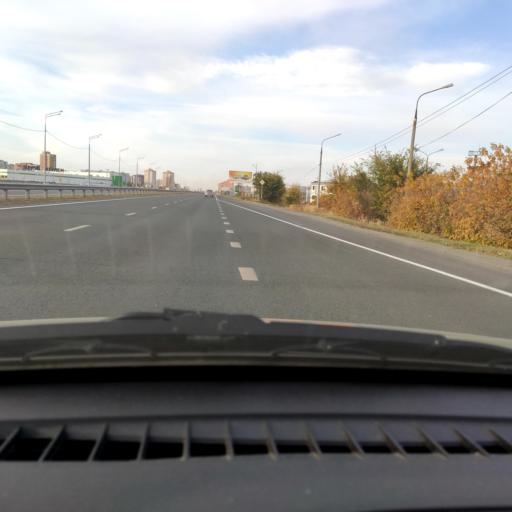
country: RU
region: Samara
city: Tol'yatti
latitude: 53.5548
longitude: 49.3446
